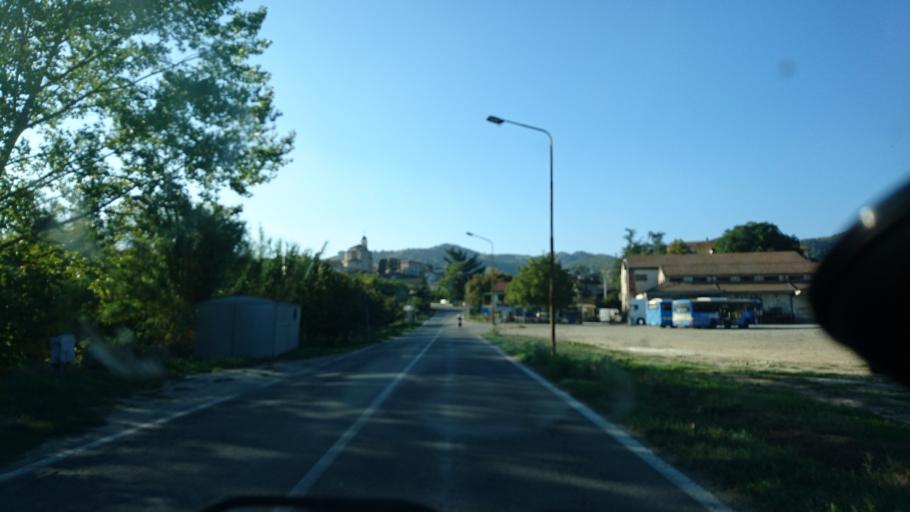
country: IT
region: Piedmont
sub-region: Provincia di Asti
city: Bubbio
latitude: 44.6618
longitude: 8.3007
